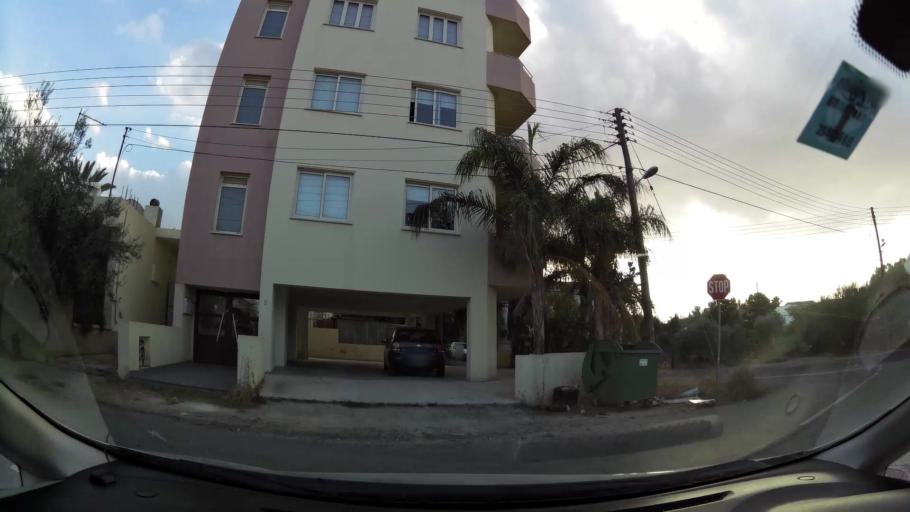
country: CY
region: Lefkosia
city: Tseri
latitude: 35.1197
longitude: 33.3124
